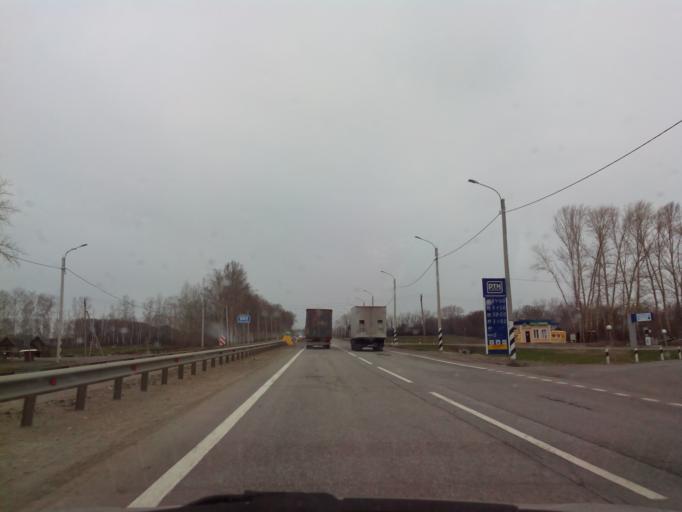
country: RU
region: Tambov
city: Selezni
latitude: 52.7473
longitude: 41.1914
